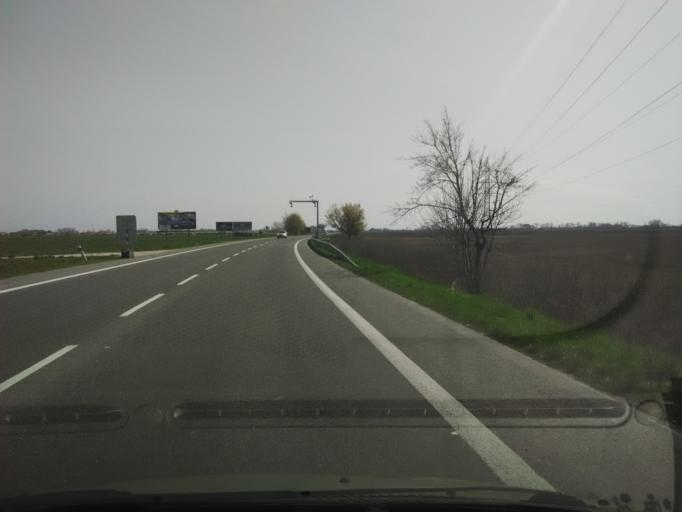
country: SK
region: Trnavsky
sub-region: Okres Galanta
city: Galanta
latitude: 48.1902
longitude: 17.7532
